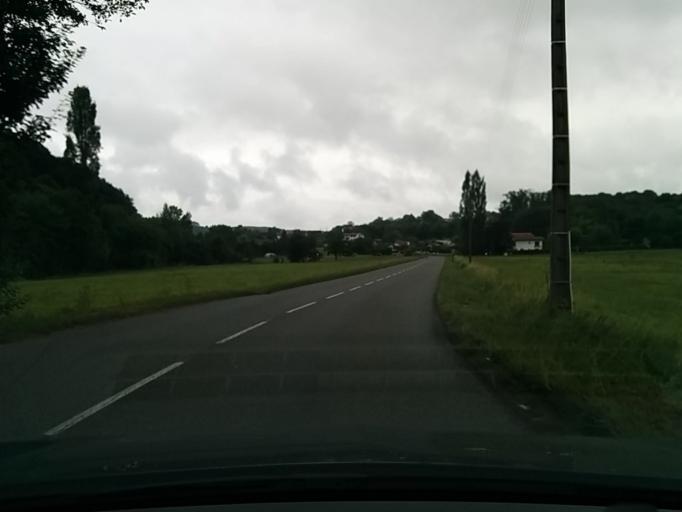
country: FR
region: Aquitaine
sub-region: Departement des Pyrenees-Atlantiques
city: Saint-Pee-sur-Nivelle
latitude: 43.3480
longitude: -1.5524
